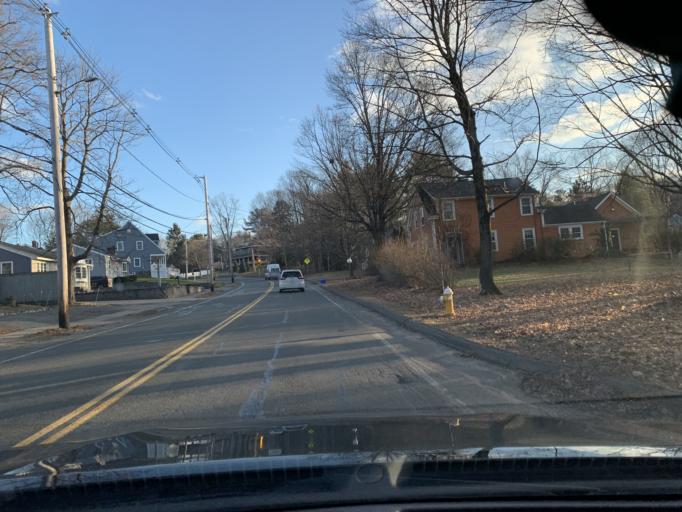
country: US
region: Massachusetts
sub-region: Essex County
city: Danvers
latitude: 42.5760
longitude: -70.9582
